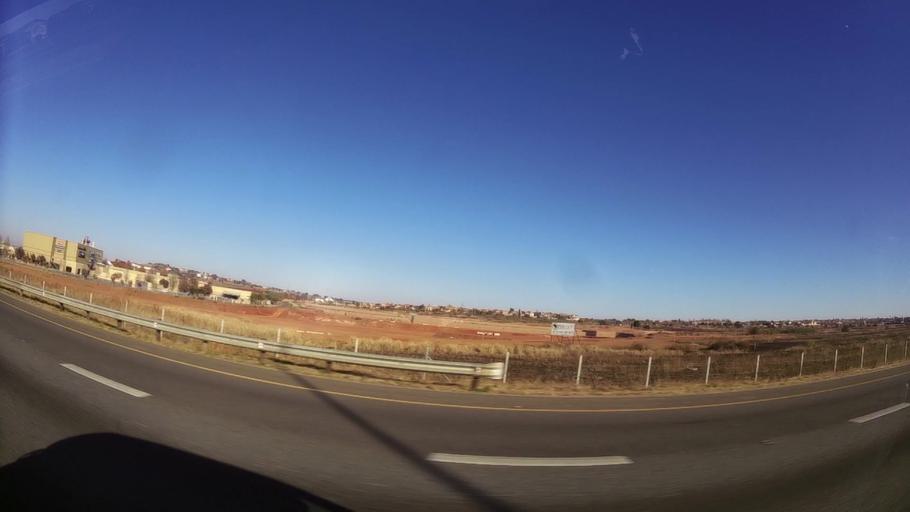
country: ZA
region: Gauteng
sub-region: City of Tshwane Metropolitan Municipality
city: Centurion
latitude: -25.8587
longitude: 28.2526
